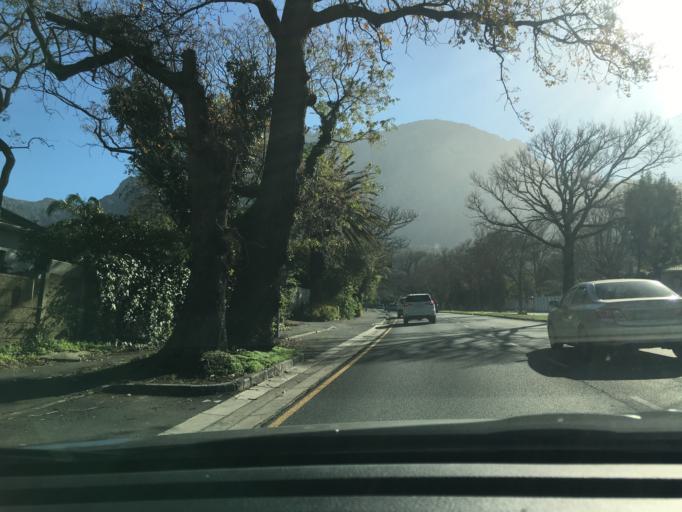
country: ZA
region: Western Cape
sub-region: City of Cape Town
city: Newlands
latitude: -33.9793
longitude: 18.4519
